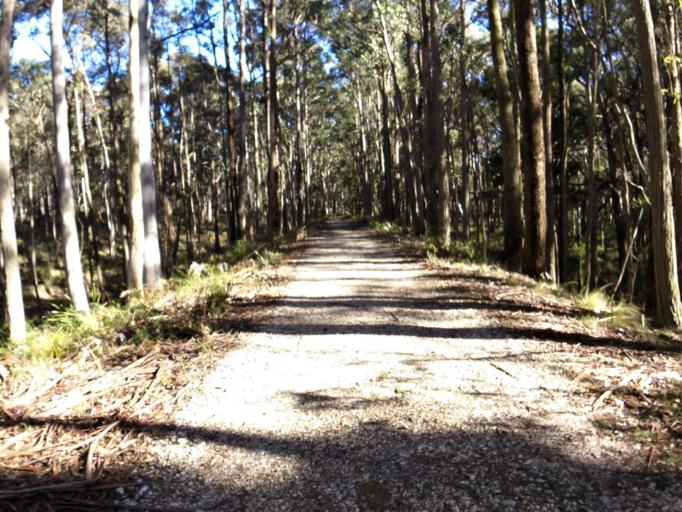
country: AU
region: Victoria
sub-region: Moorabool
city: Bacchus Marsh
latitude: -37.3922
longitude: 144.2823
